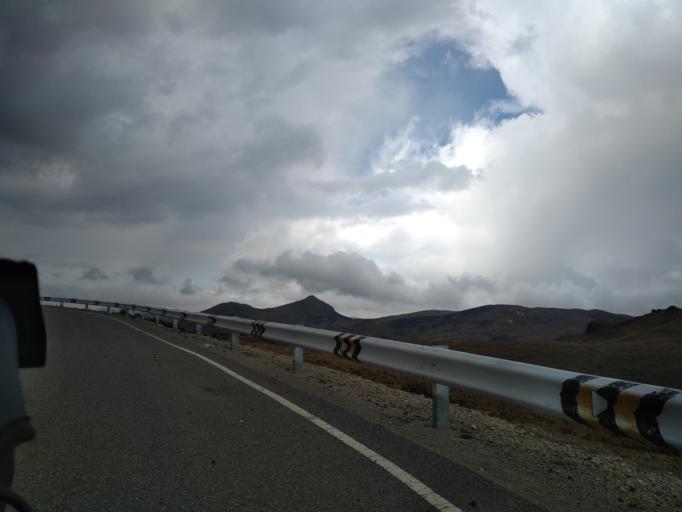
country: PE
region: La Libertad
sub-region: Provincia de Santiago de Chuco
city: Quiruvilca
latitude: -7.9932
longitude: -78.2961
